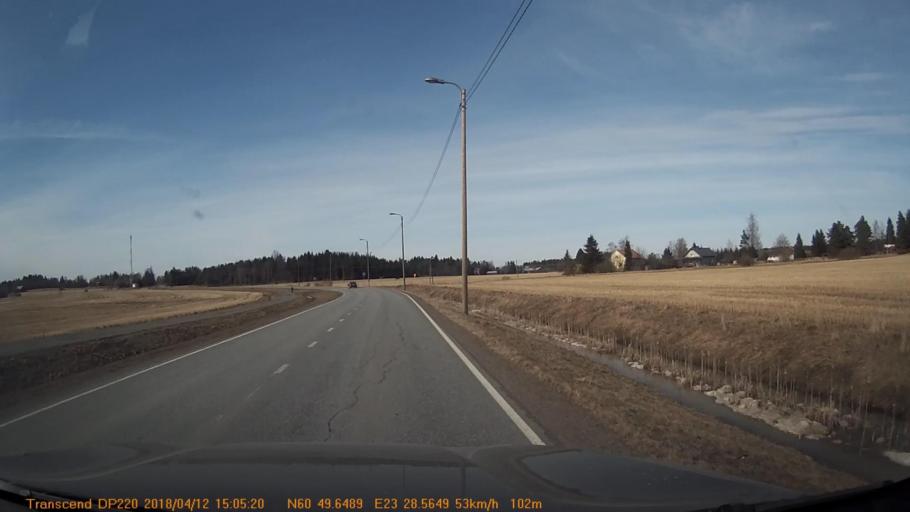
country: FI
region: Haeme
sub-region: Forssa
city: Jokioinen
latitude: 60.8277
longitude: 23.4760
